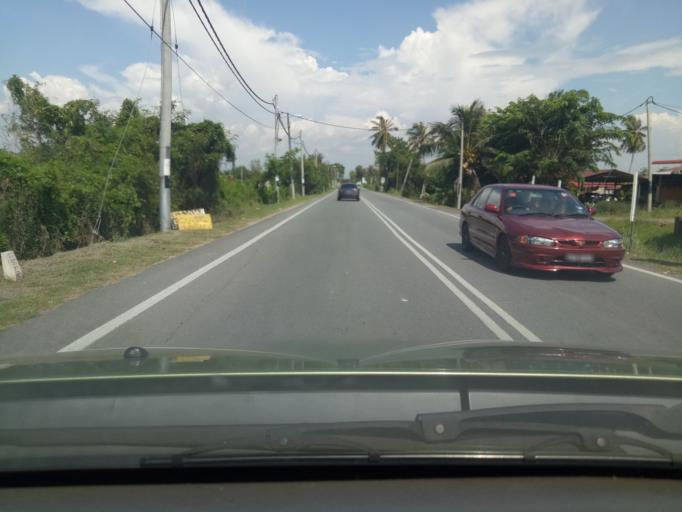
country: MY
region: Kedah
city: Alor Setar
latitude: 5.9743
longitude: 100.4042
